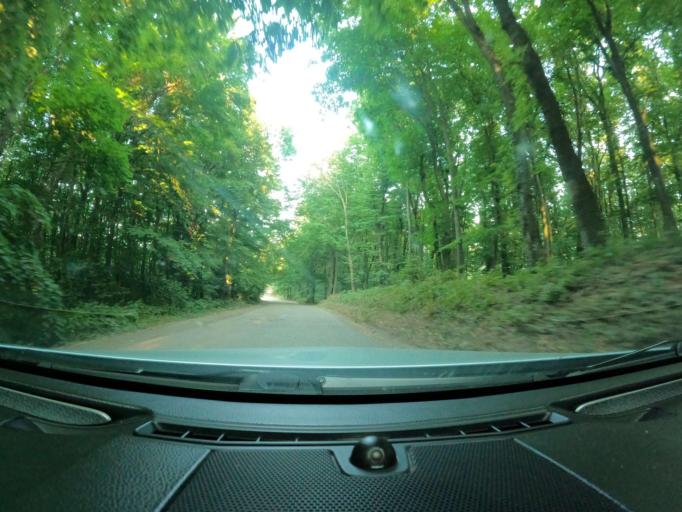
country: RS
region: Autonomna Pokrajina Vojvodina
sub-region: Juznobacki Okrug
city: Beocin
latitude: 45.1554
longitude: 19.7218
